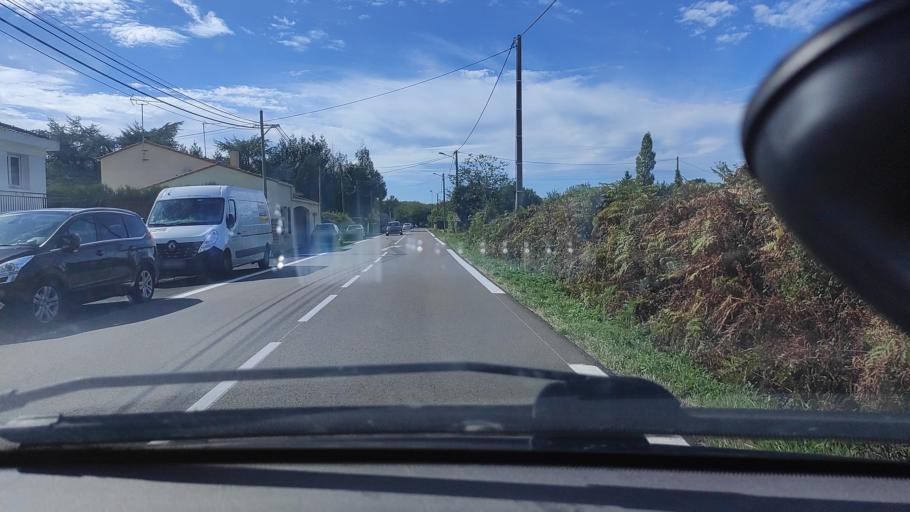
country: FR
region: Pays de la Loire
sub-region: Departement de la Vendee
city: La Boissiere-des-Landes
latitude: 46.5590
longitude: -1.4474
